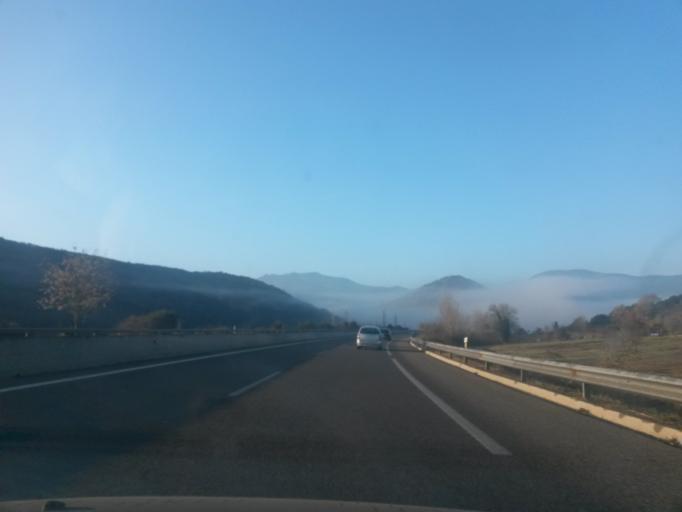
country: ES
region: Catalonia
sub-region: Provincia de Girona
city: Argelaguer
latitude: 42.2138
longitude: 2.6266
